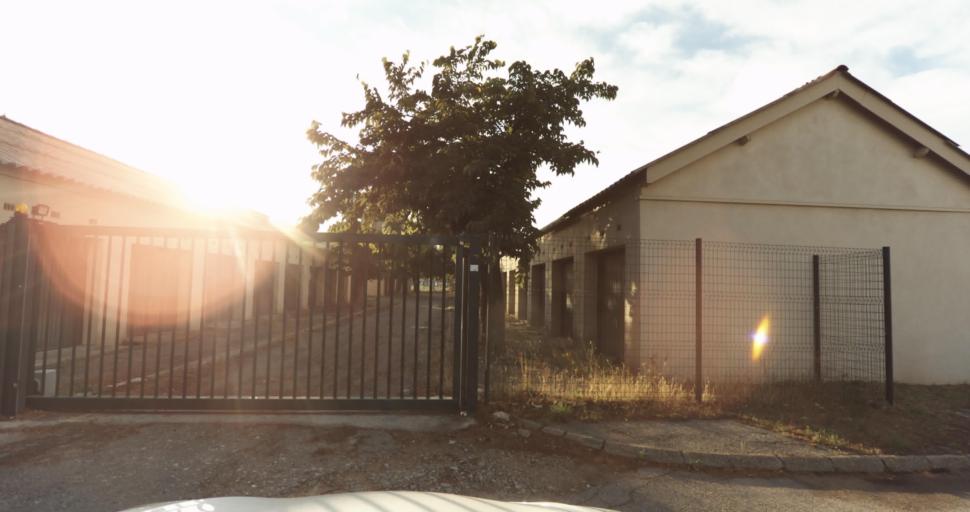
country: FR
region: Provence-Alpes-Cote d'Azur
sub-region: Departement des Bouches-du-Rhone
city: Miramas
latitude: 43.5833
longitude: 4.9902
